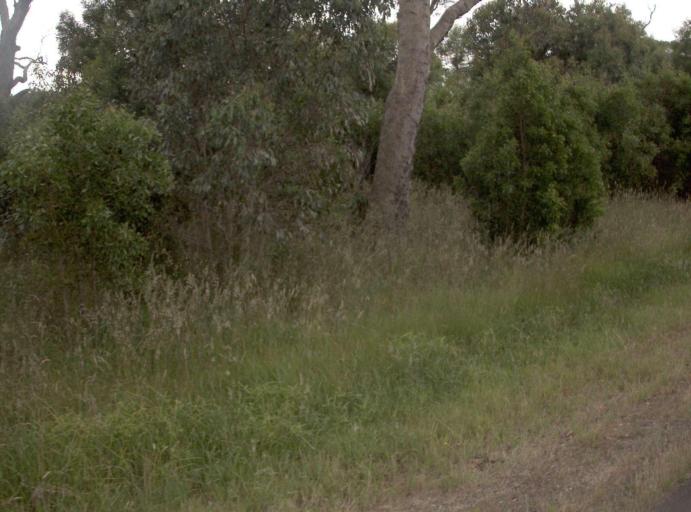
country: AU
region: Victoria
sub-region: Latrobe
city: Traralgon
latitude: -38.5577
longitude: 146.8096
